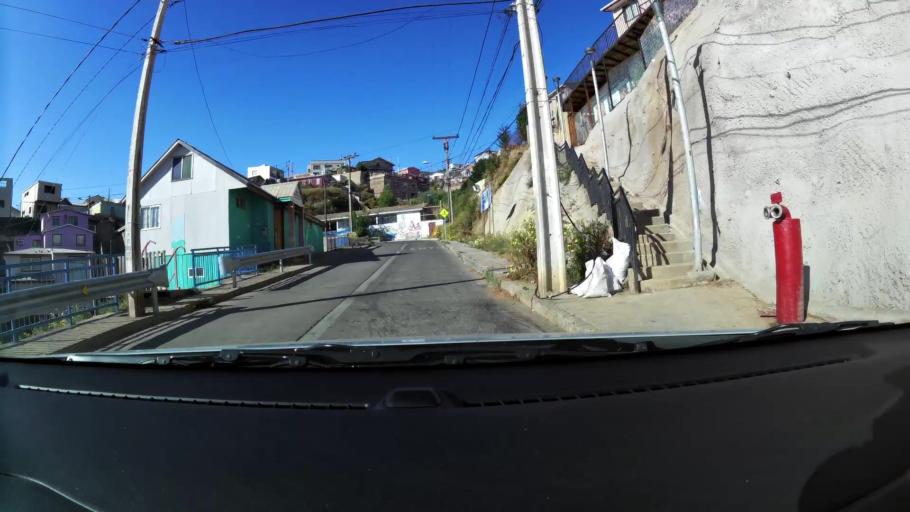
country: CL
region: Valparaiso
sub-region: Provincia de Valparaiso
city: Valparaiso
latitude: -33.0614
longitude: -71.6070
